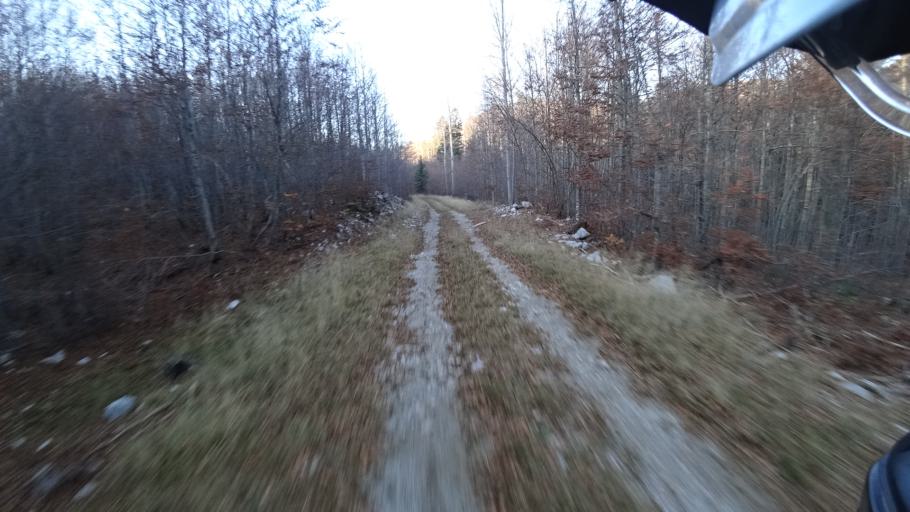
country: HR
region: Primorsko-Goranska
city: Drazice
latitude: 45.4864
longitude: 14.4818
